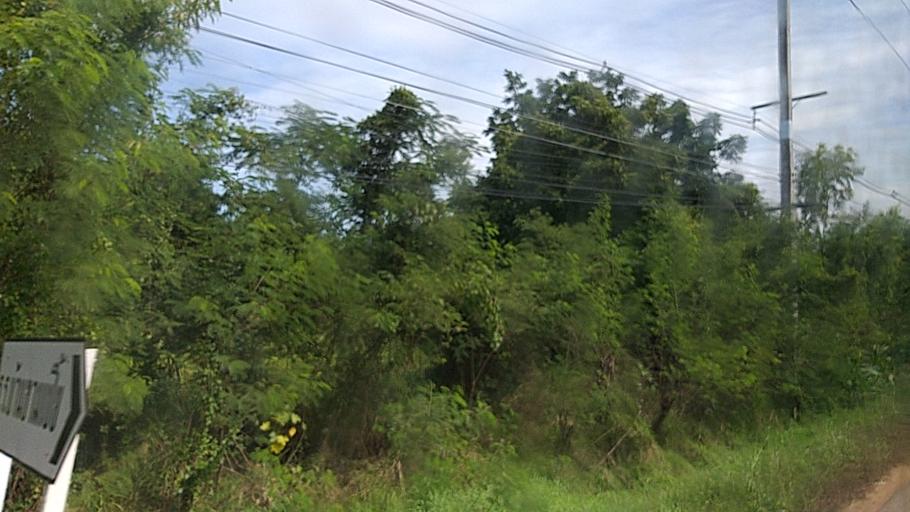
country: TH
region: Maha Sarakham
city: Chiang Yuen
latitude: 16.4432
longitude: 102.9942
